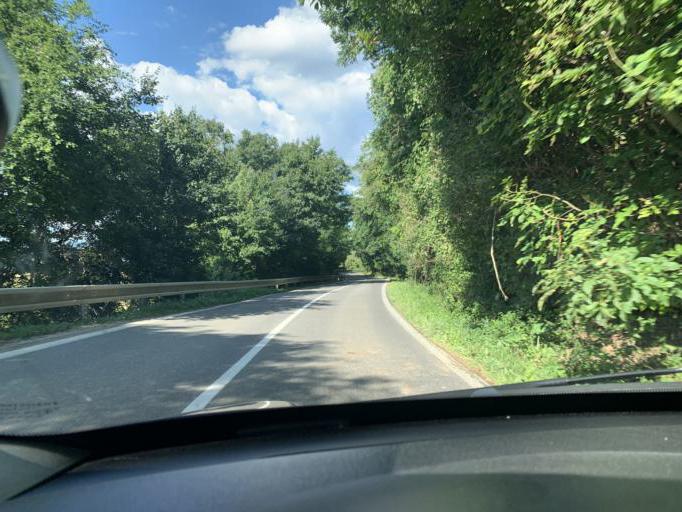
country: SK
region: Trenciansky
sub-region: Okres Nove Mesto nad Vahom
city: Nove Mesto nad Vahom
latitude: 48.8004
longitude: 17.9072
